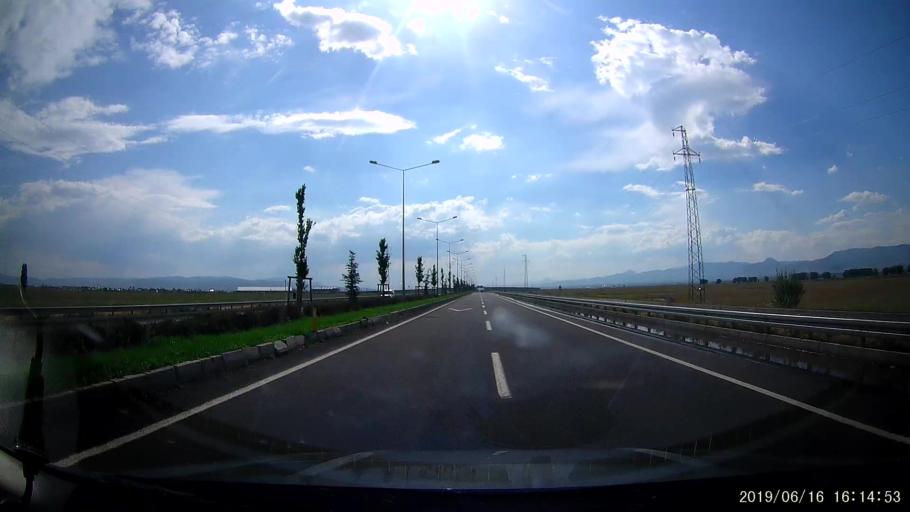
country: TR
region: Erzurum
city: Erzurum
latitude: 39.9613
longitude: 41.2379
